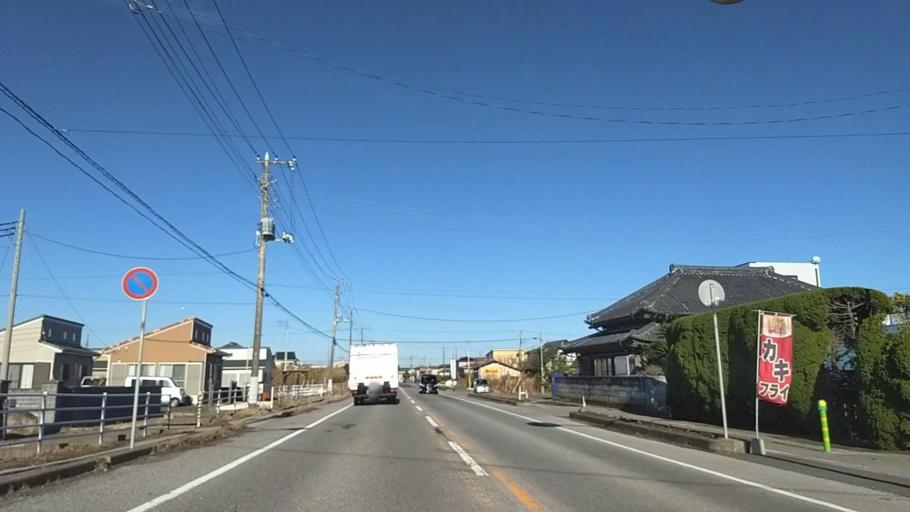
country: JP
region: Chiba
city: Togane
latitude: 35.5215
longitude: 140.4431
